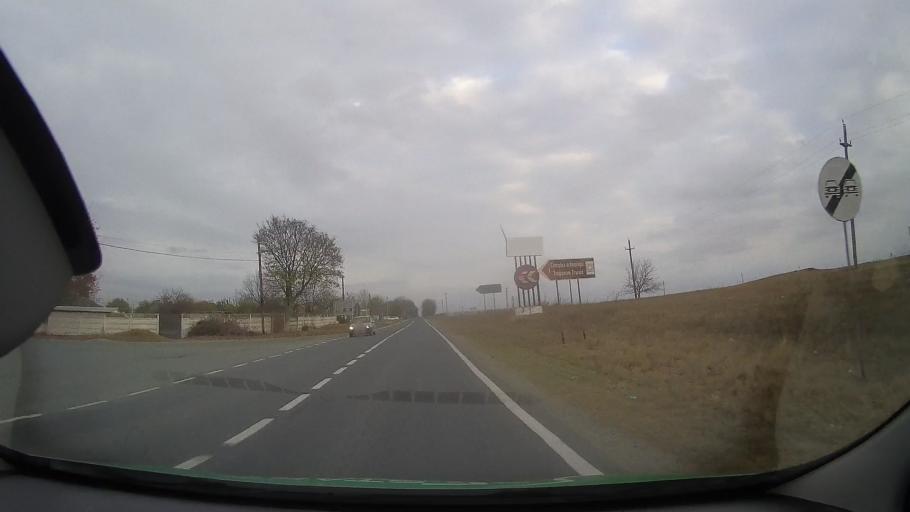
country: RO
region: Constanta
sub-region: Comuna Adamclisi
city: Adamclisi
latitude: 44.0886
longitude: 27.9633
